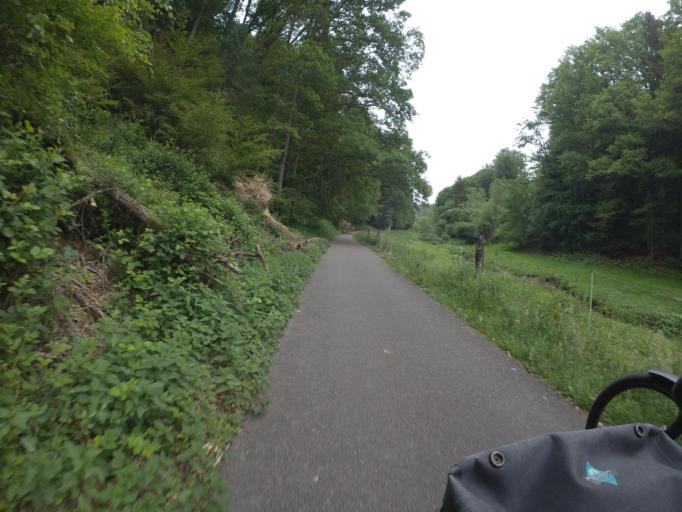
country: DE
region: Rheinland-Pfalz
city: Horbach
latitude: 49.3276
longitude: 7.6492
